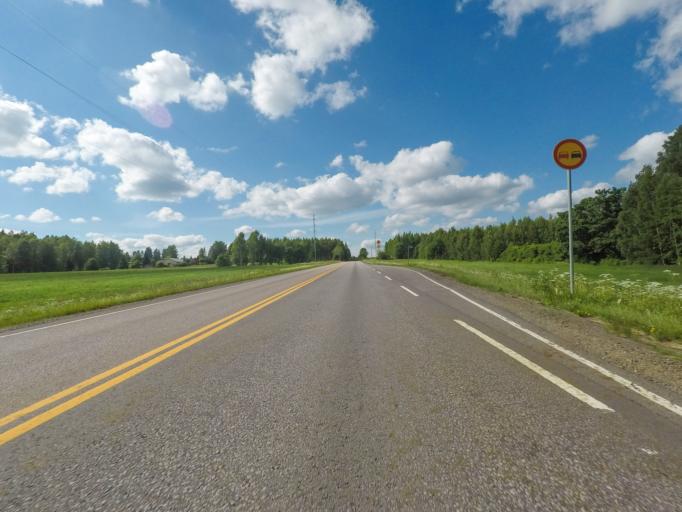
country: FI
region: Southern Savonia
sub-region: Savonlinna
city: Kerimaeki
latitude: 61.8673
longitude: 29.1335
